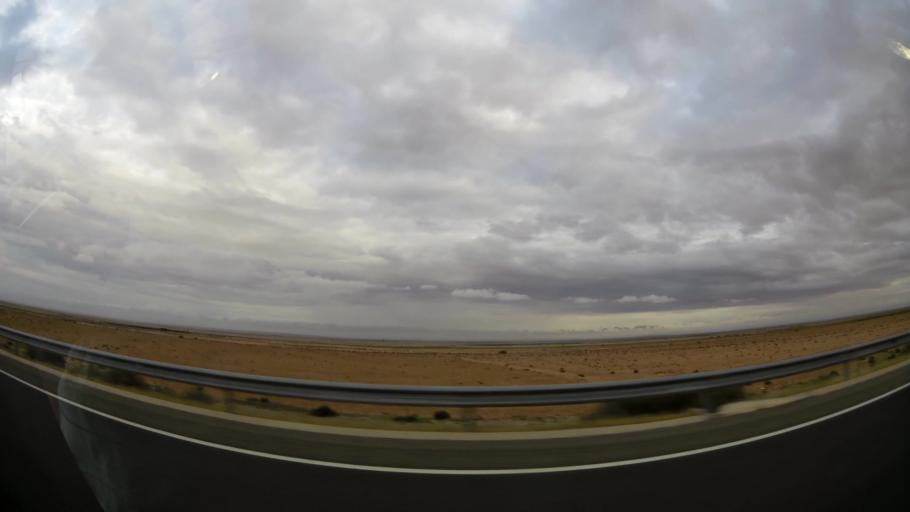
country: MA
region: Taza-Al Hoceima-Taounate
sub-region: Taza
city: Guercif
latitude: 34.3258
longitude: -3.5610
